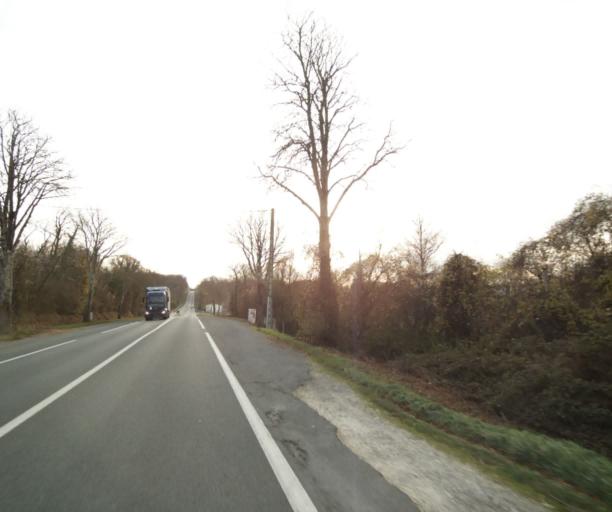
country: FR
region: Poitou-Charentes
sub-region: Departement de la Charente-Maritime
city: Fontcouverte
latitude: 45.7969
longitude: -0.5662
